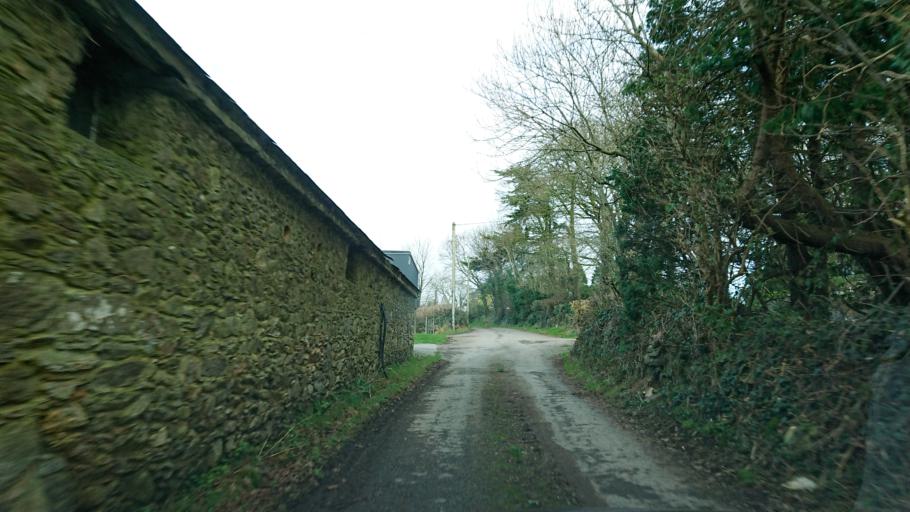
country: IE
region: Munster
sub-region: Waterford
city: Tra Mhor
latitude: 52.1649
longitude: -7.2743
